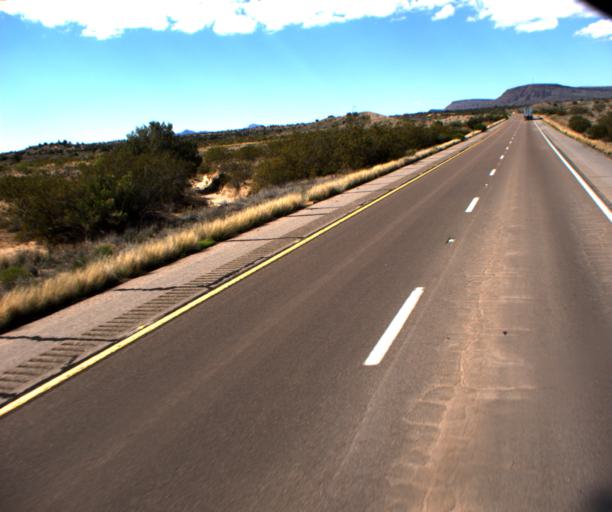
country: US
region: Arizona
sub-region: Mohave County
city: Kingman
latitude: 35.1226
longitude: -113.6663
